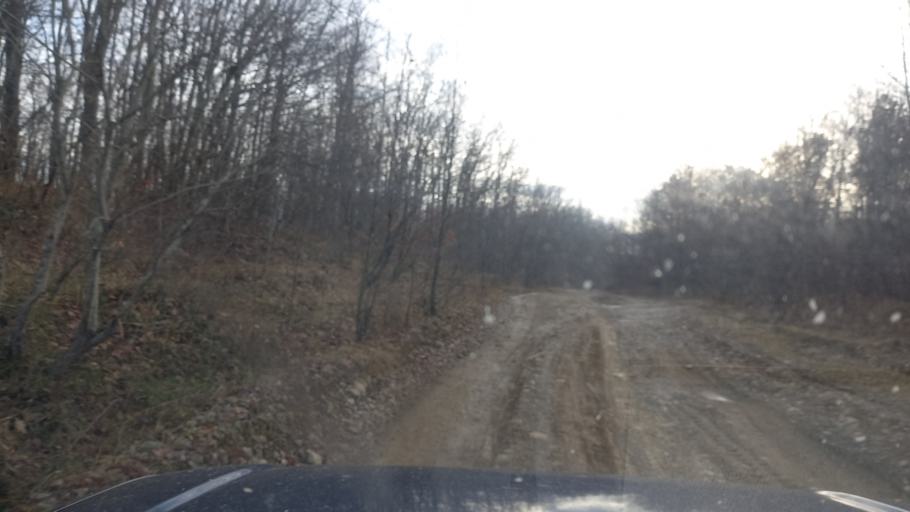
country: RU
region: Krasnodarskiy
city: Neftegorsk
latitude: 44.2370
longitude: 39.7784
